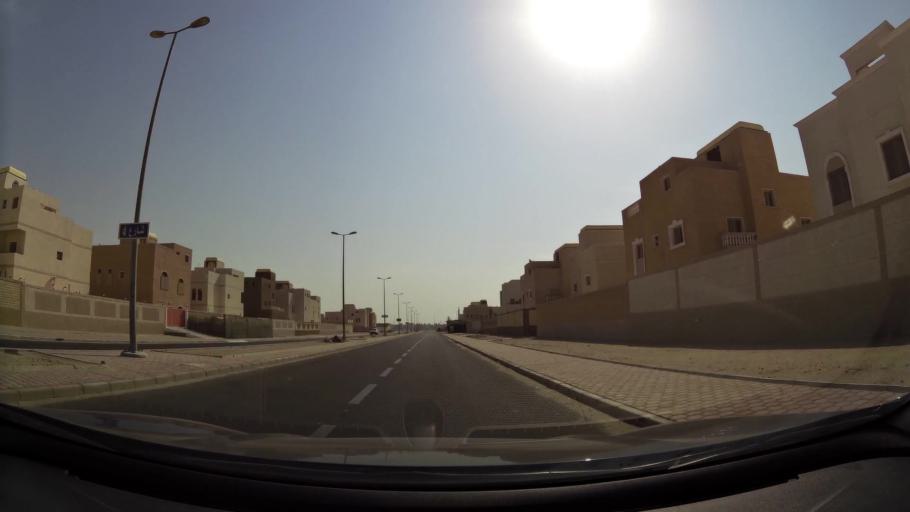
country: KW
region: Al Ahmadi
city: Al Wafrah
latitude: 28.7936
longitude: 48.0724
